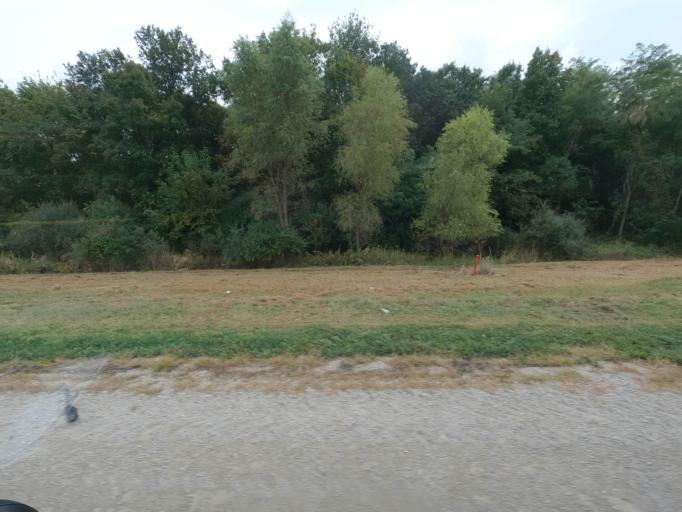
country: US
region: Iowa
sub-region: Wapello County
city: Ottumwa
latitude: 41.0963
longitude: -92.4708
